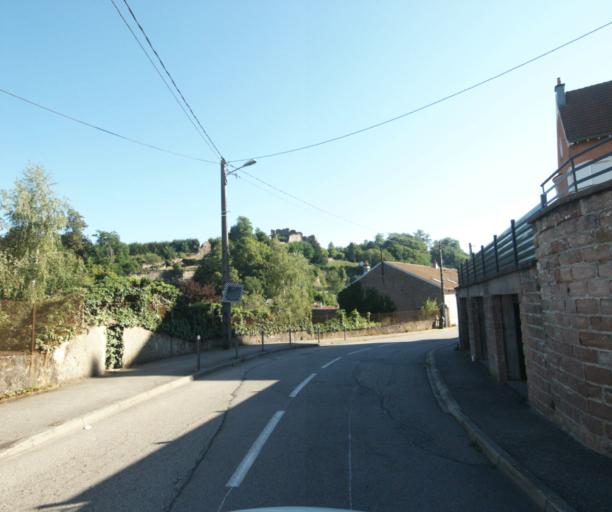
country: FR
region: Lorraine
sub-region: Departement des Vosges
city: Epinal
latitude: 48.1731
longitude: 6.4545
